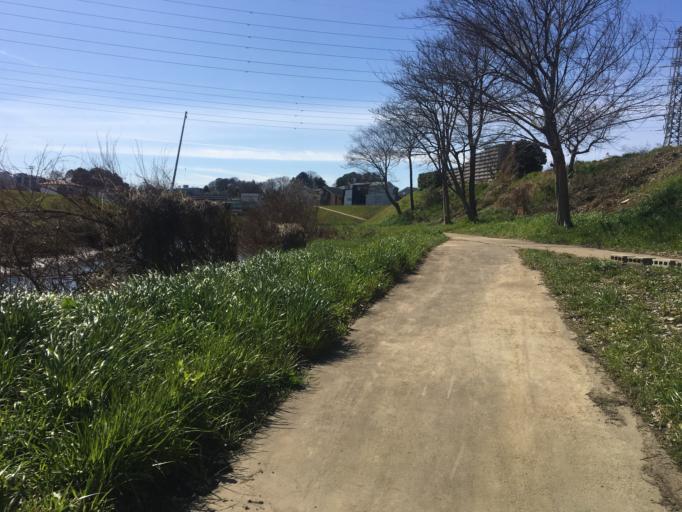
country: JP
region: Saitama
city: Asaka
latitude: 35.8127
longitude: 139.6093
